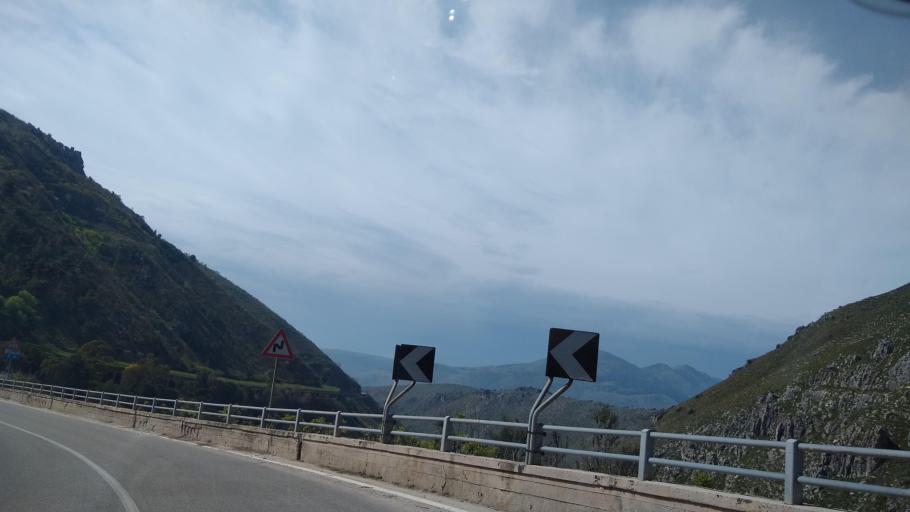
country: IT
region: Sicily
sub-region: Palermo
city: Montelepre
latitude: 38.0520
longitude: 13.1854
